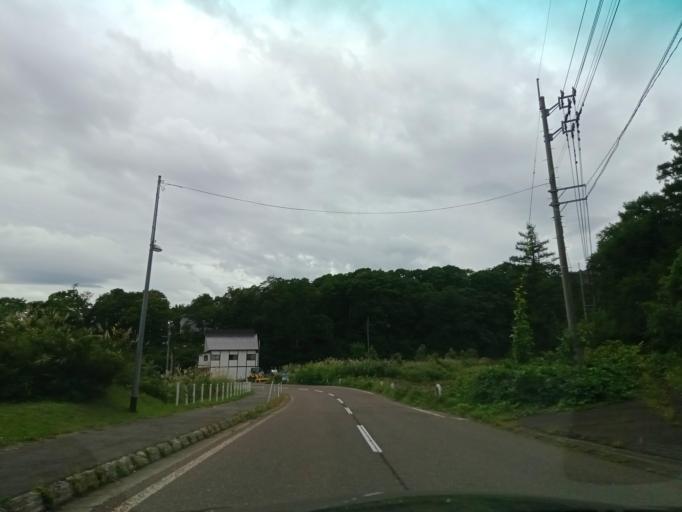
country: JP
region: Niigata
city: Arai
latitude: 36.8891
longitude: 138.1766
